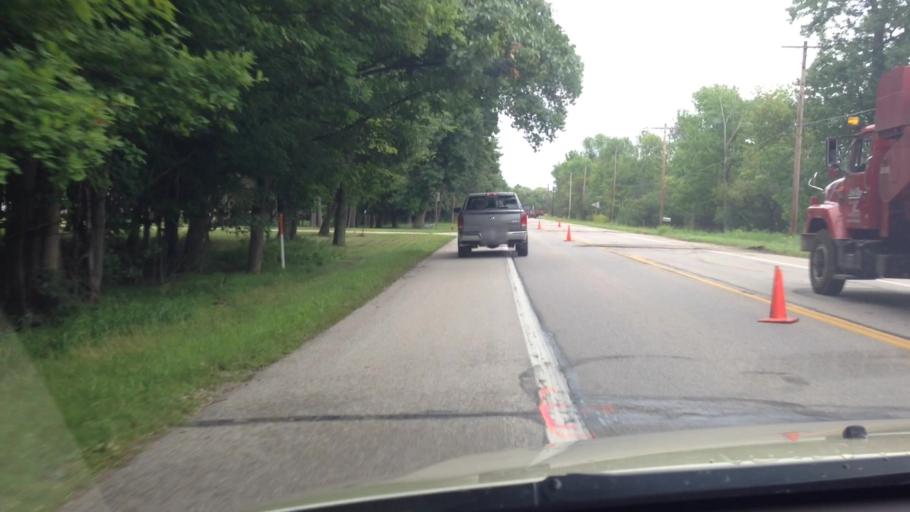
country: US
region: Michigan
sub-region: Delta County
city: Escanaba
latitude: 45.7084
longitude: -87.0976
